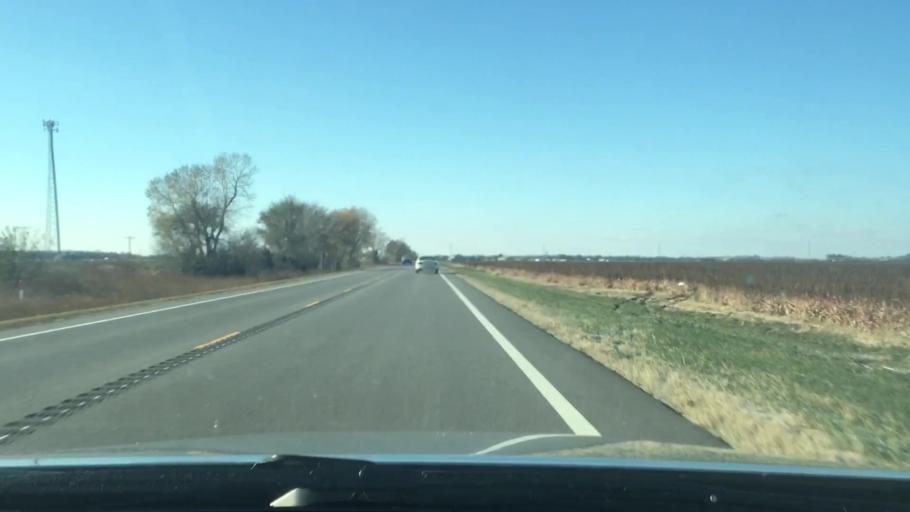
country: US
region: Kansas
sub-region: Reno County
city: Nickerson
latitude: 38.1270
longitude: -98.0539
